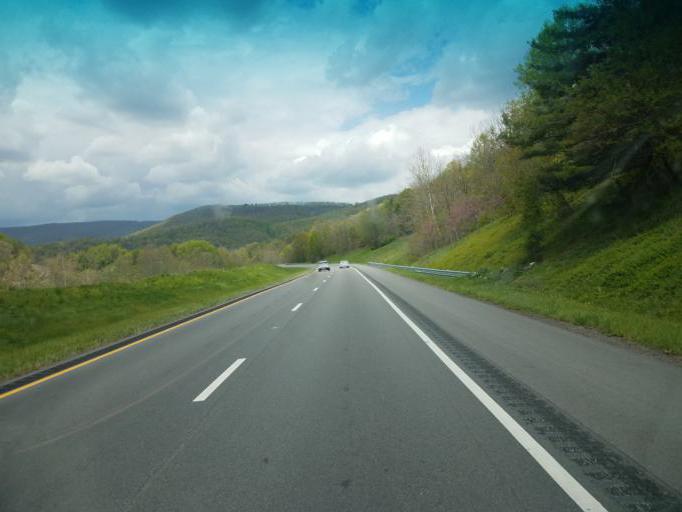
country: US
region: West Virginia
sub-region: Mercer County
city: Bluefield
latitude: 37.2329
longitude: -81.0956
